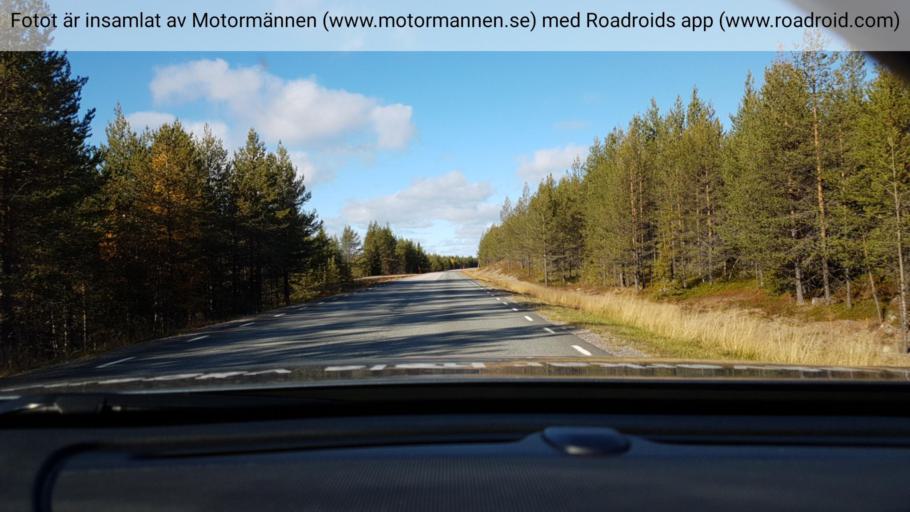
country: SE
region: Norrbotten
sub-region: Arvidsjaurs Kommun
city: Arvidsjaur
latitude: 65.7299
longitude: 18.6547
